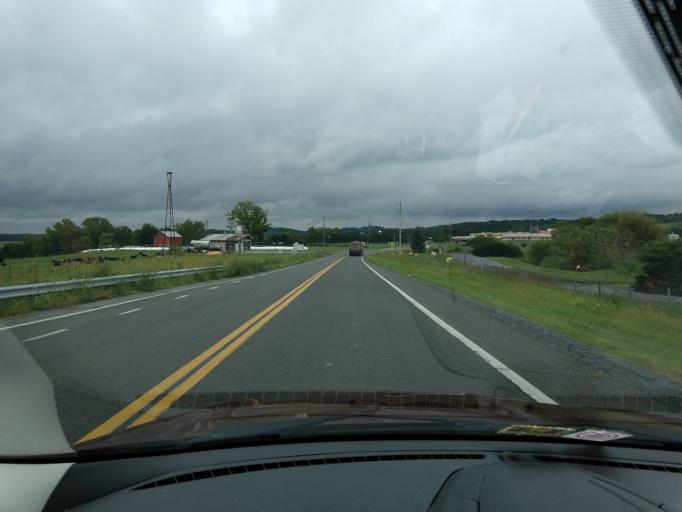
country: US
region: Virginia
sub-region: Shenandoah County
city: Mount Jackson
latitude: 38.7042
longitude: -78.6580
